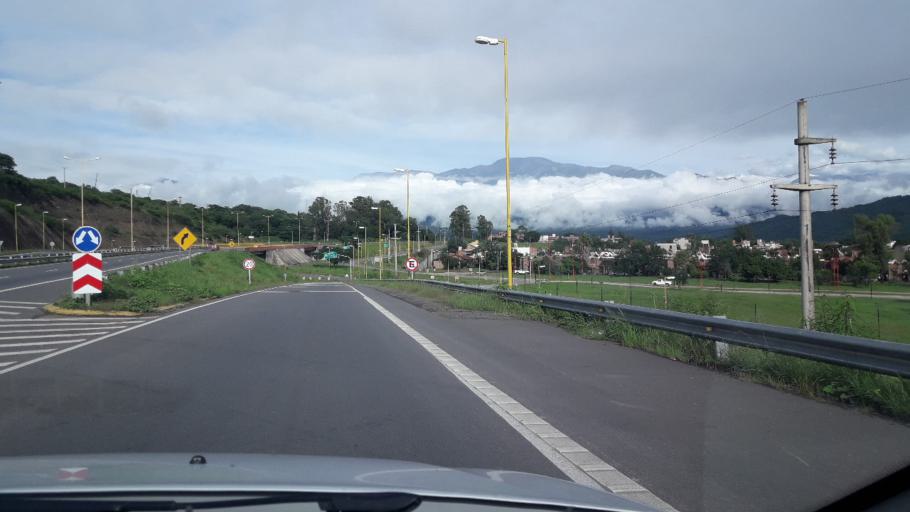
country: AR
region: Jujuy
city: San Salvador de Jujuy
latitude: -24.1854
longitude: -65.3312
